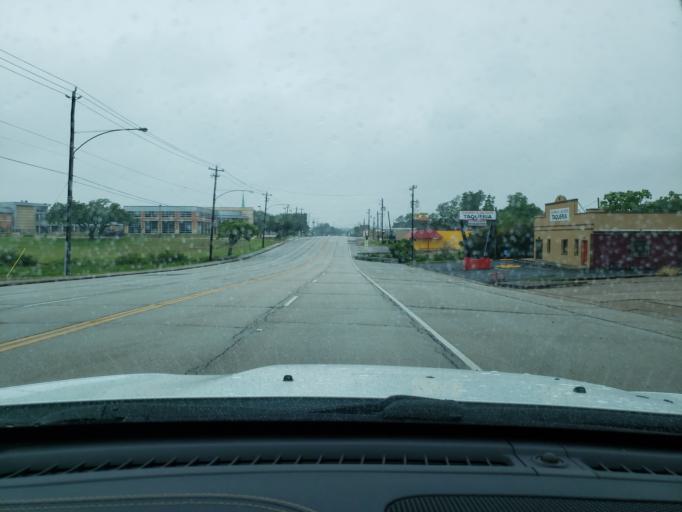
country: US
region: Texas
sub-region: Harris County
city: Baytown
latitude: 29.7342
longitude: -94.9801
